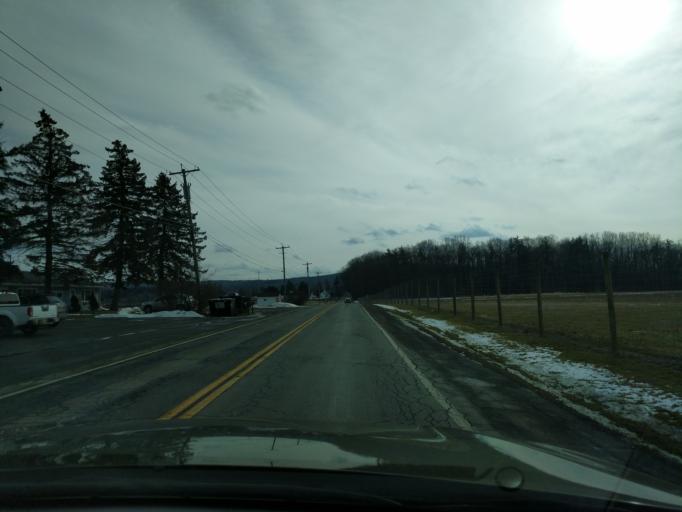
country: US
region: New York
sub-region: Tompkins County
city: Northeast Ithaca
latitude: 42.4505
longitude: -76.4495
